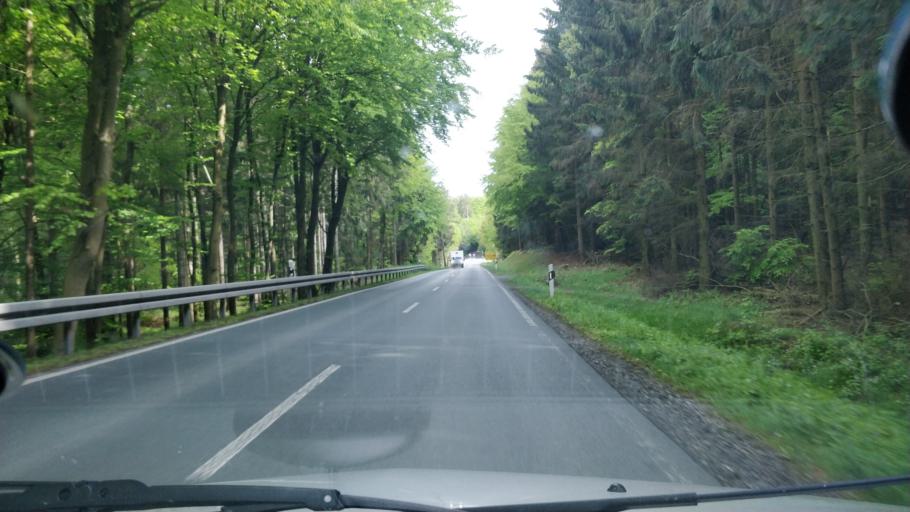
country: DE
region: Hesse
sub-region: Regierungsbezirk Darmstadt
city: Neu-Anspach
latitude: 50.3329
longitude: 8.4942
